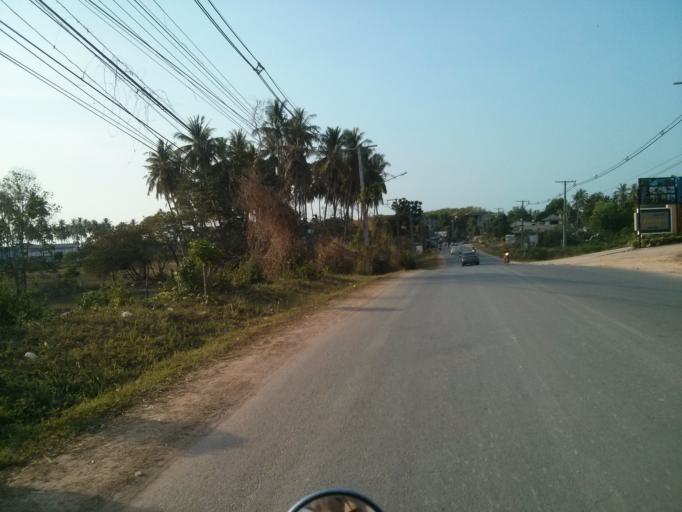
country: TH
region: Krabi
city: Saladan
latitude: 7.5788
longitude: 99.0343
